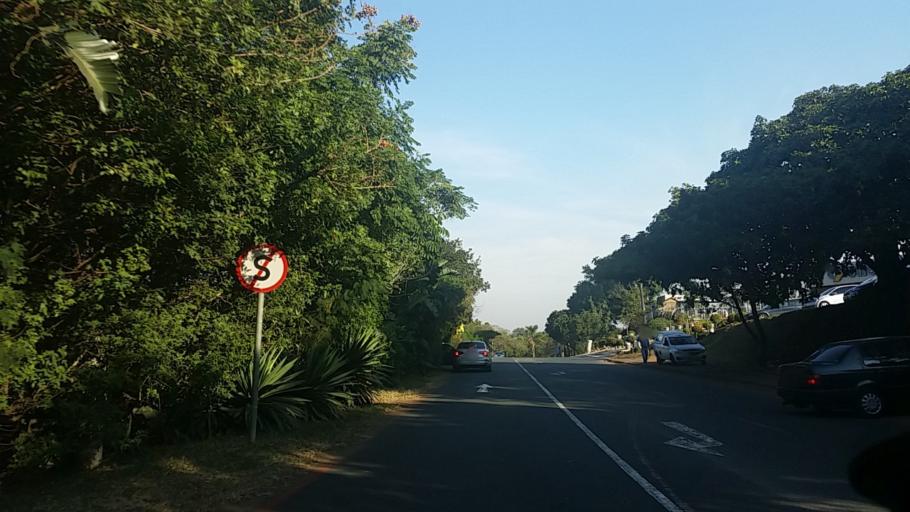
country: ZA
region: KwaZulu-Natal
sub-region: eThekwini Metropolitan Municipality
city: Berea
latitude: -29.8360
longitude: 30.9195
